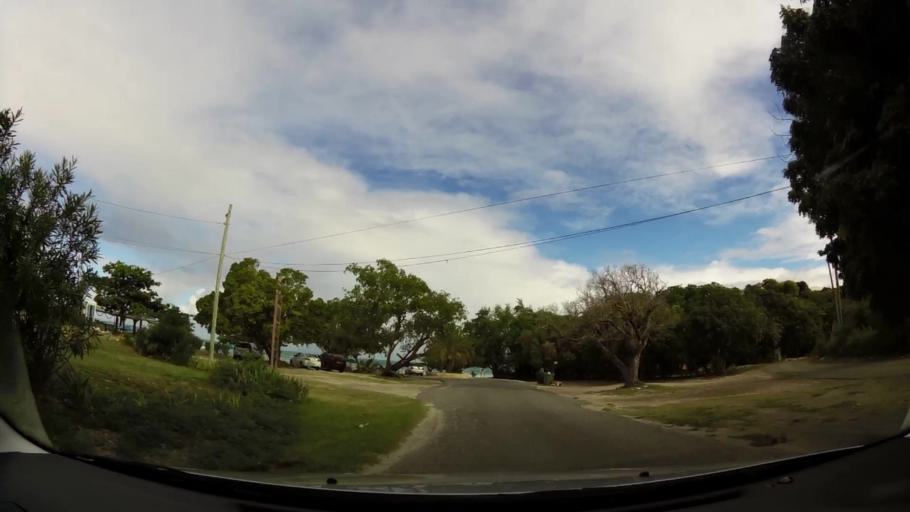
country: AG
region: Saint Peter
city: Parham
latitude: 17.0986
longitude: -61.6891
